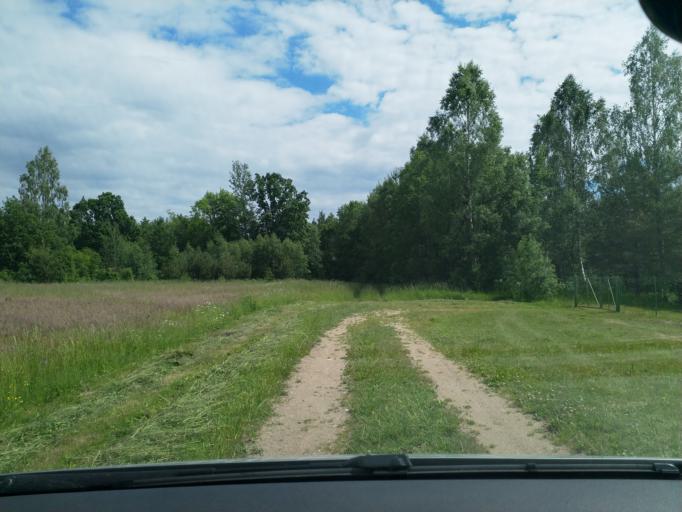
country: LV
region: Kuldigas Rajons
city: Kuldiga
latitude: 56.8374
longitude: 21.9491
